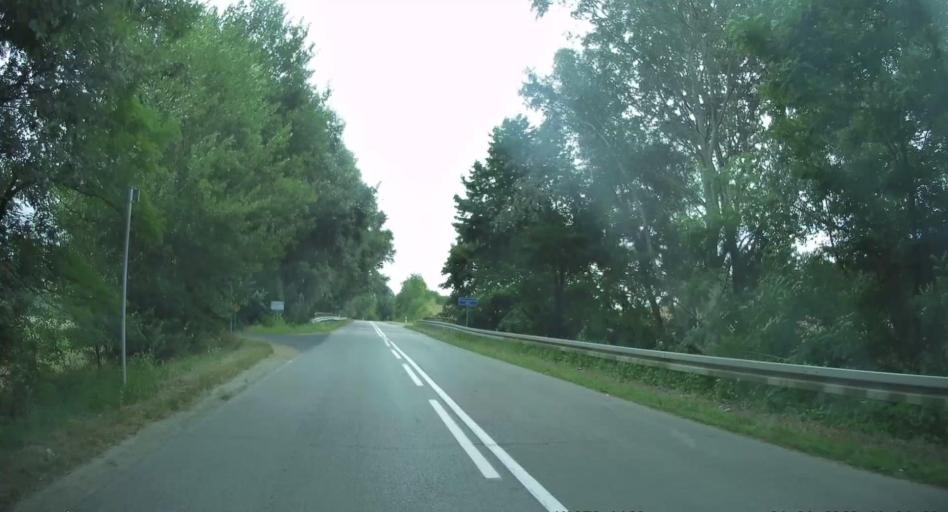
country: PL
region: Swietokrzyskie
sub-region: Powiat sandomierski
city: Klimontow
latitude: 50.6673
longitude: 21.4154
